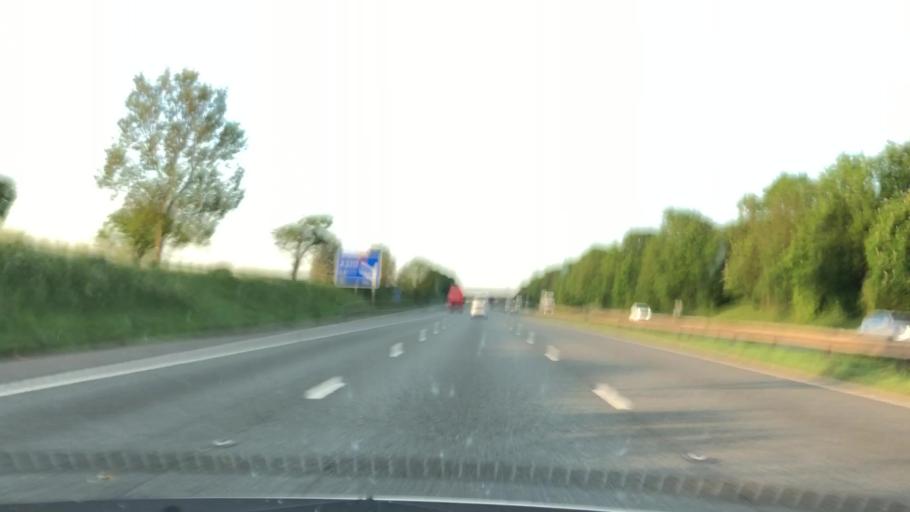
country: GB
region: England
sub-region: Cheshire West and Chester
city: Elton
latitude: 53.2560
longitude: -2.8307
